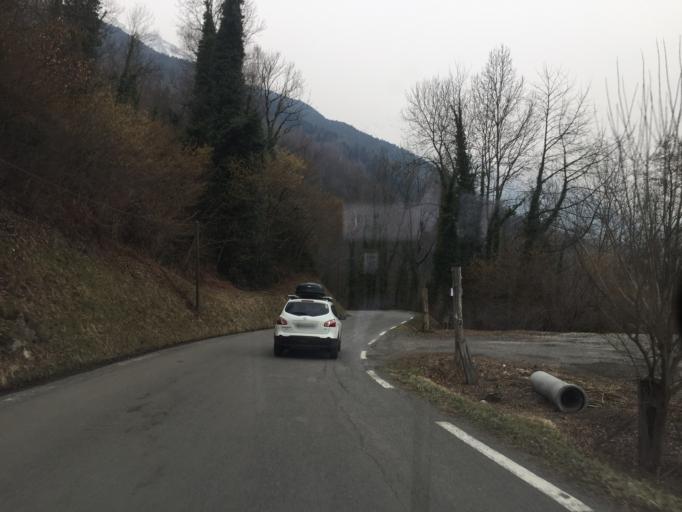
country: FR
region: Midi-Pyrenees
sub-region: Departement des Hautes-Pyrenees
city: Saint-Lary-Soulan
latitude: 42.8154
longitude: 0.3272
